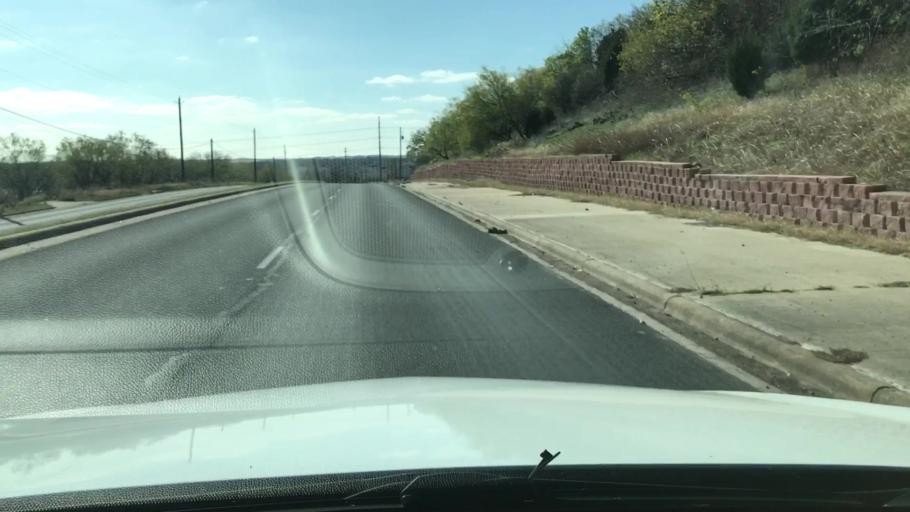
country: US
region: Texas
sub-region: Travis County
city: Onion Creek
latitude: 30.1697
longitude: -97.7227
